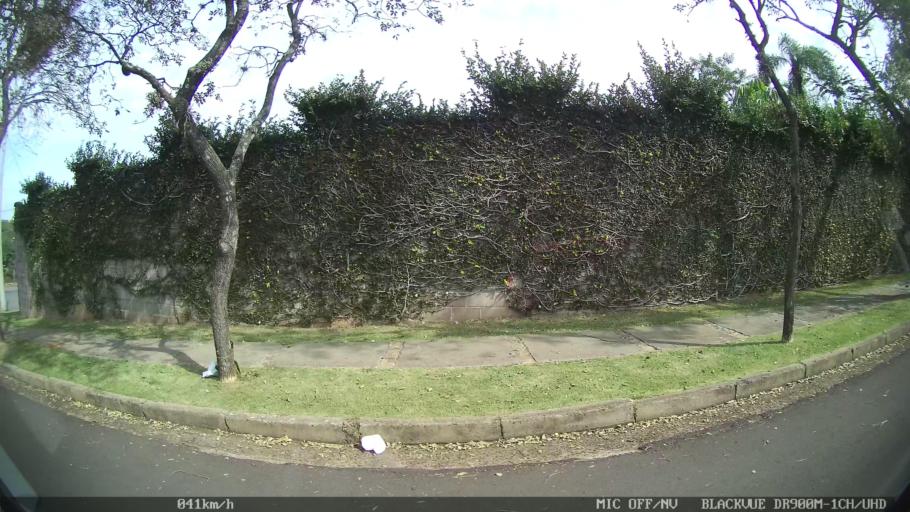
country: BR
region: Sao Paulo
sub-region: Piracicaba
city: Piracicaba
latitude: -22.7230
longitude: -47.6672
